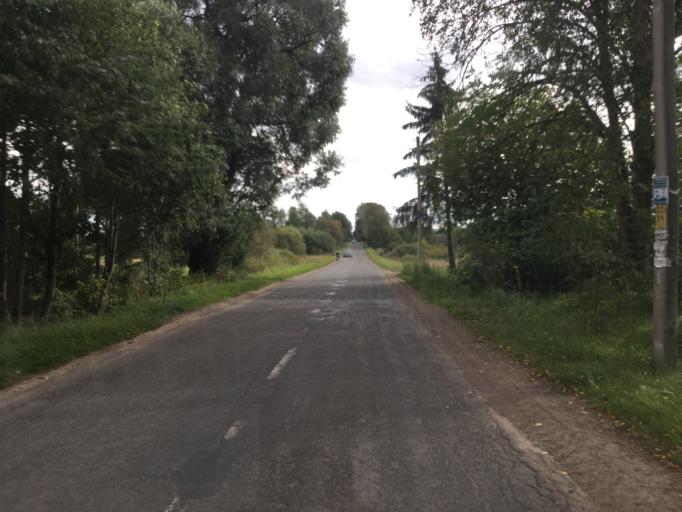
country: BY
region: Vitebsk
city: Vitebsk
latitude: 55.1482
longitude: 30.2796
